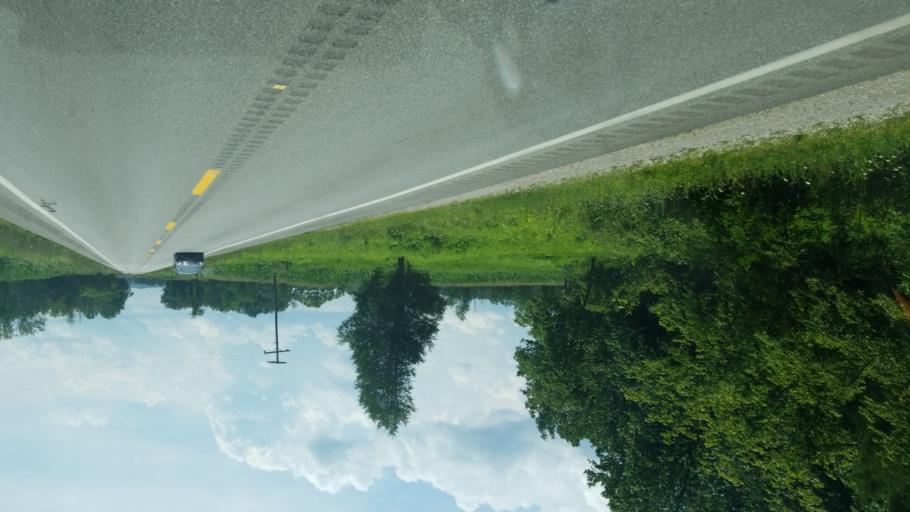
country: US
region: West Virginia
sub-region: Putnam County
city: Buffalo
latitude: 38.6889
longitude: -81.9651
